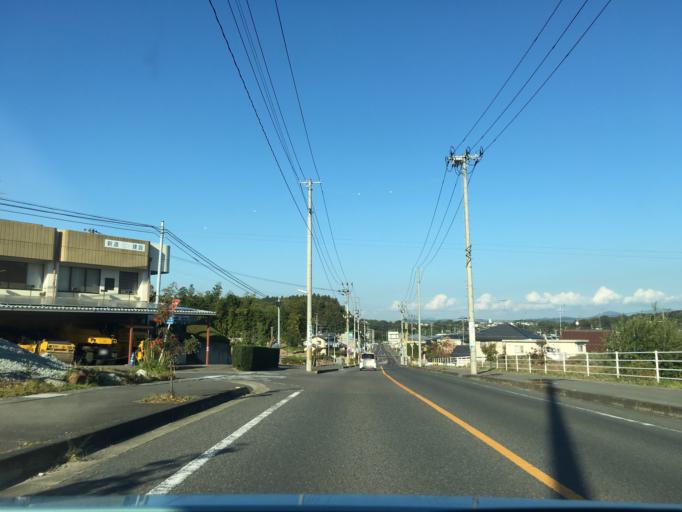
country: JP
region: Fukushima
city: Sukagawa
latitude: 37.3063
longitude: 140.3725
